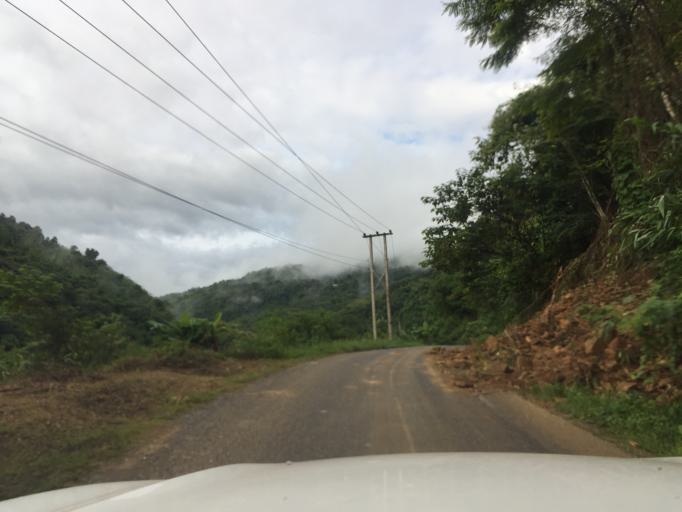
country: LA
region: Oudomxai
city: Muang La
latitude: 21.0918
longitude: 102.2455
